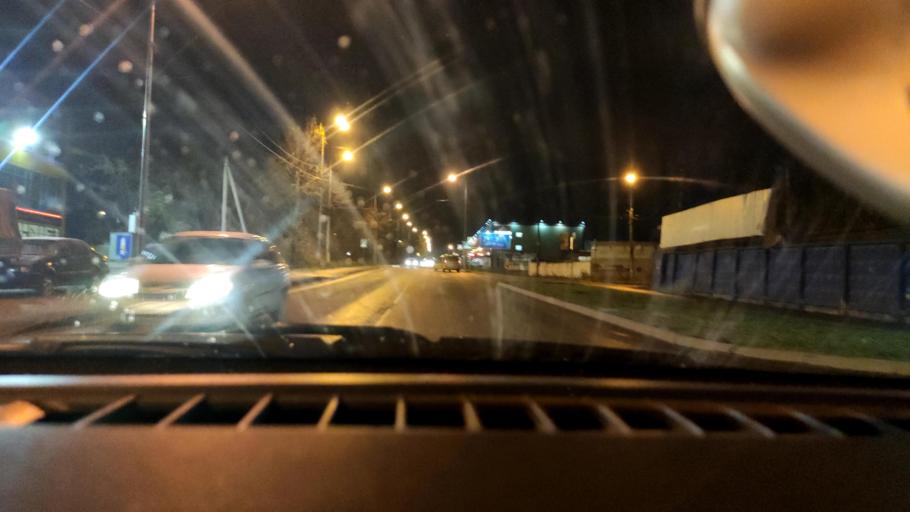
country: RU
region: Perm
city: Kondratovo
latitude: 57.9627
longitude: 56.1587
